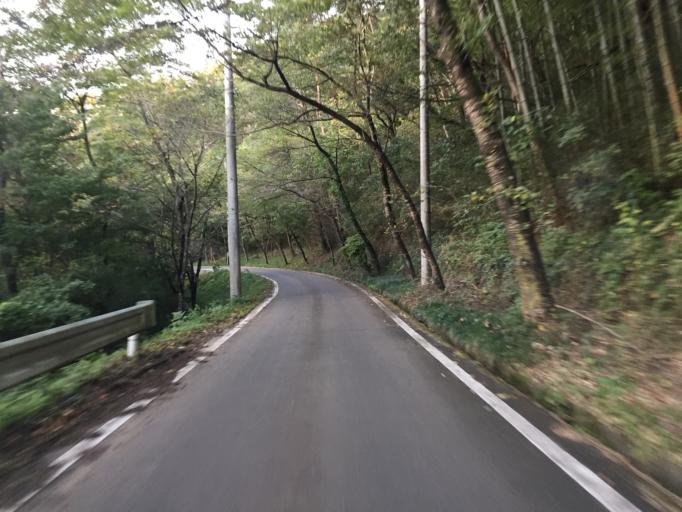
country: JP
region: Fukushima
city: Yanagawamachi-saiwaicho
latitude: 37.8516
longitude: 140.6312
